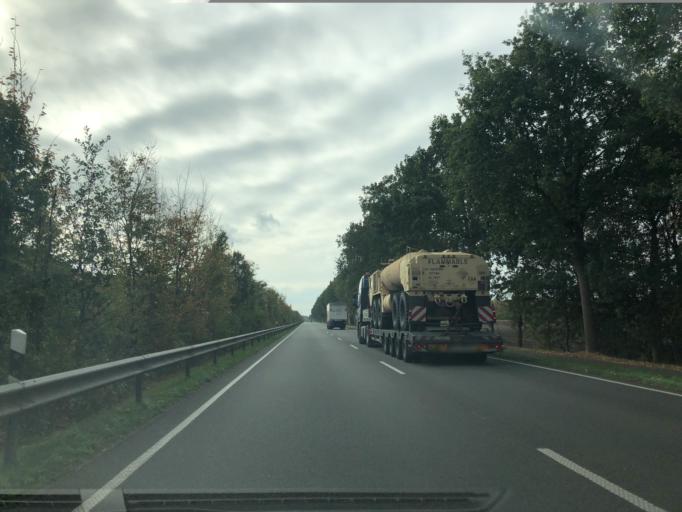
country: DE
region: Lower Saxony
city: Friesoythe
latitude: 53.0520
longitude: 7.7990
